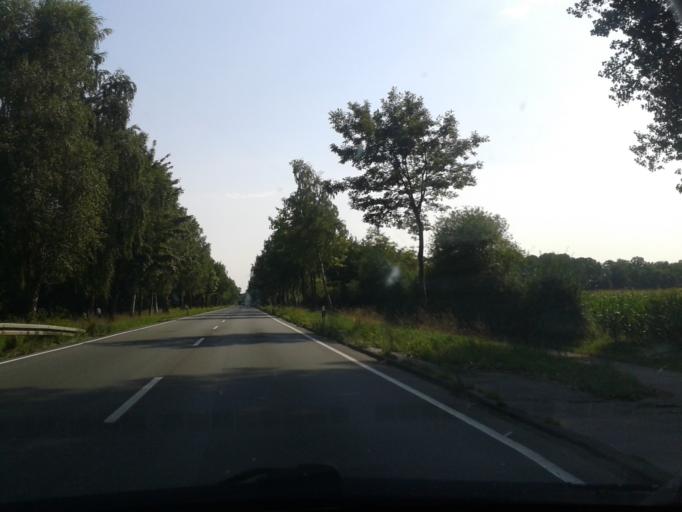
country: DE
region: North Rhine-Westphalia
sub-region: Regierungsbezirk Detmold
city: Delbruck
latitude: 51.7457
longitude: 8.5615
